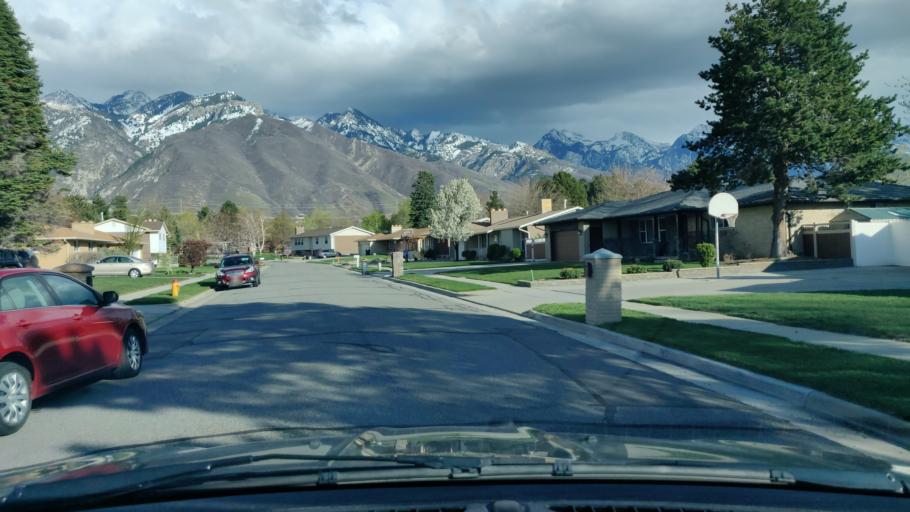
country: US
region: Utah
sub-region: Salt Lake County
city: Cottonwood Heights
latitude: 40.6197
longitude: -111.8180
